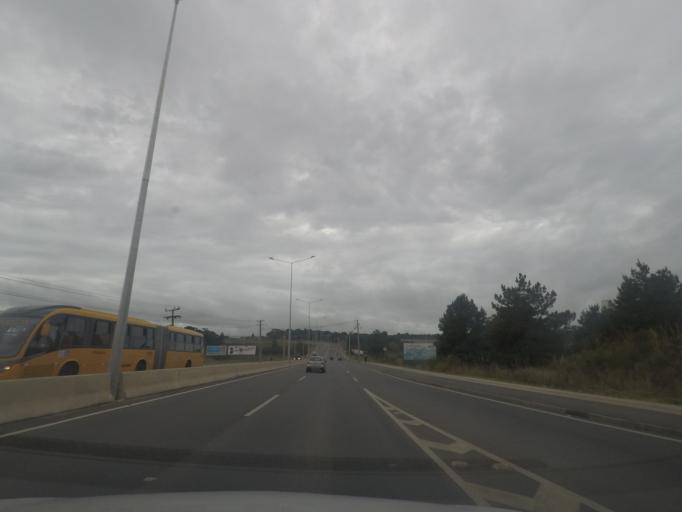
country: BR
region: Parana
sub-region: Piraquara
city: Piraquara
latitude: -25.4610
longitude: -49.0859
